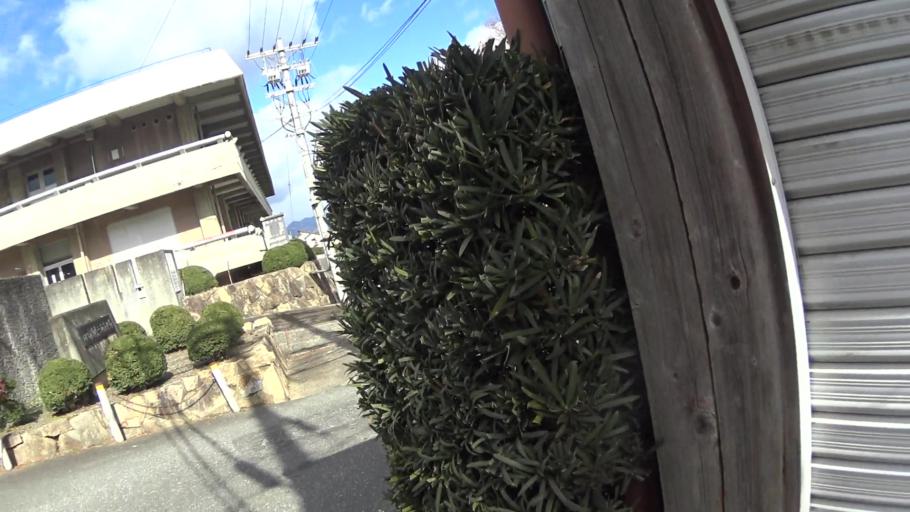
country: JP
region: Kyoto
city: Muko
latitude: 34.9563
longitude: 135.6949
